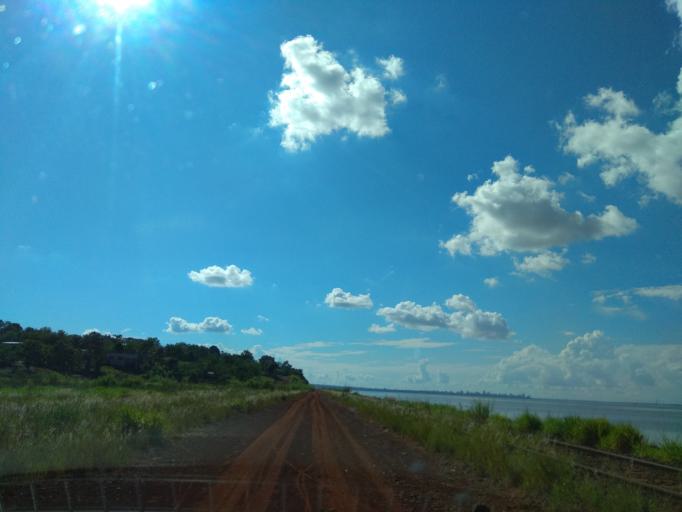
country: AR
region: Misiones
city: Garupa
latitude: -27.4503
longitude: -55.8362
